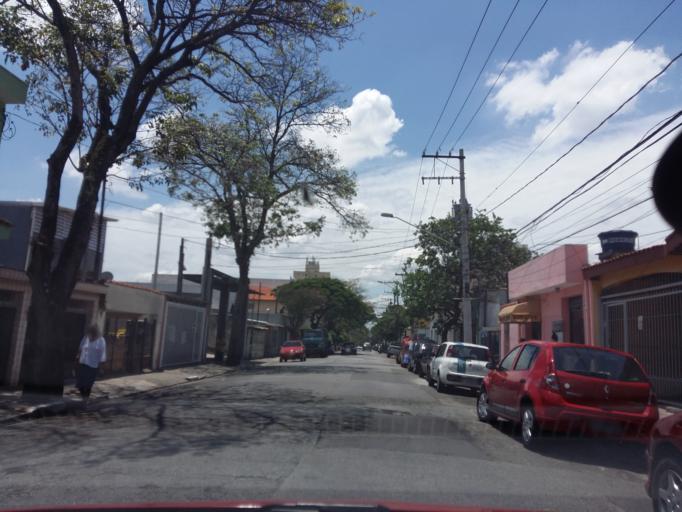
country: BR
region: Sao Paulo
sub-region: Sao Caetano Do Sul
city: Sao Caetano do Sul
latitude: -23.6265
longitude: -46.6083
